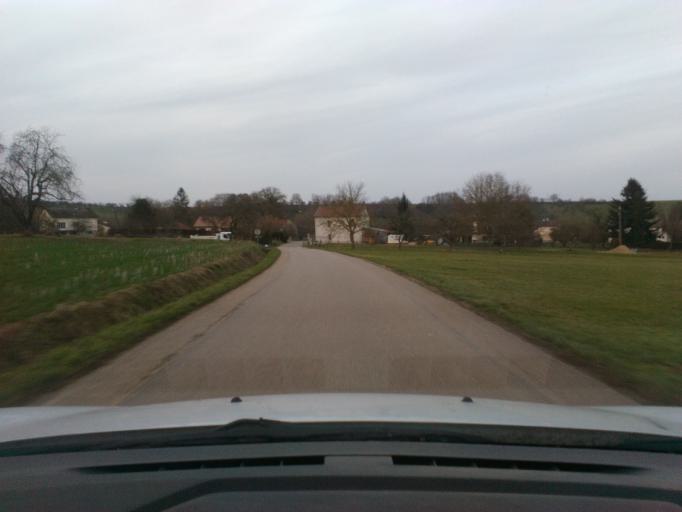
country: FR
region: Lorraine
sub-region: Departement des Vosges
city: Mirecourt
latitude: 48.3078
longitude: 6.0989
